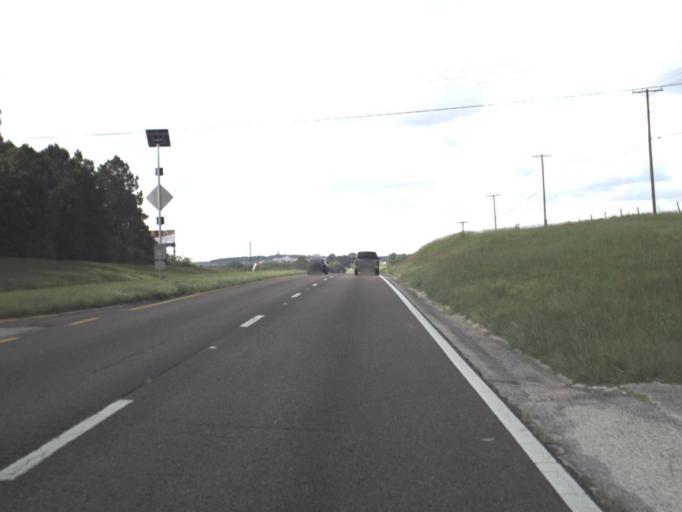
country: US
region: Florida
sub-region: Pasco County
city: Zephyrhills North
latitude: 28.2979
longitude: -82.1878
